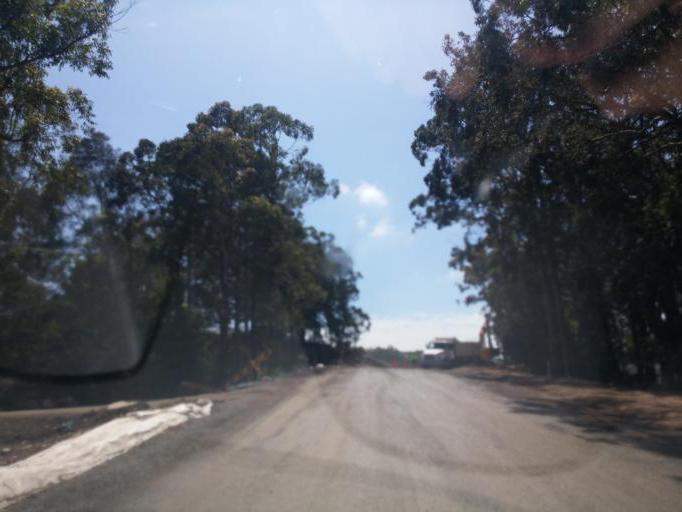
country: AU
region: New South Wales
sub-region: Great Lakes
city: Forster
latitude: -32.3883
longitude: 152.4434
